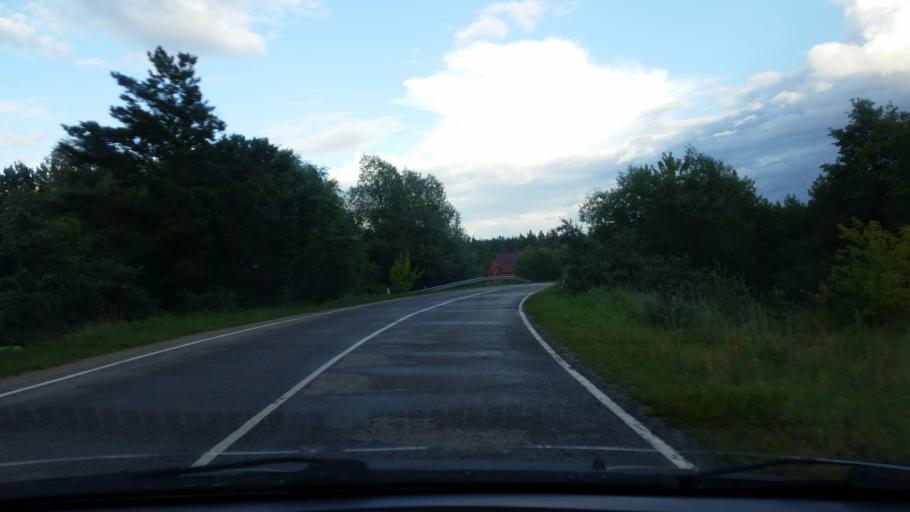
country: RU
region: Moskovskaya
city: Zhilevo
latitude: 54.8675
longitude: 37.8520
